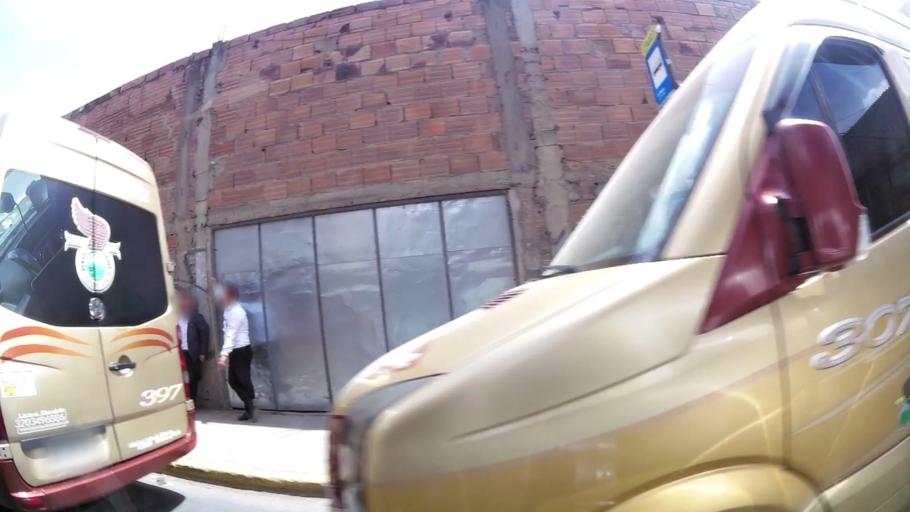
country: CO
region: Bogota D.C.
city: Bogota
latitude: 4.6514
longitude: -74.1384
